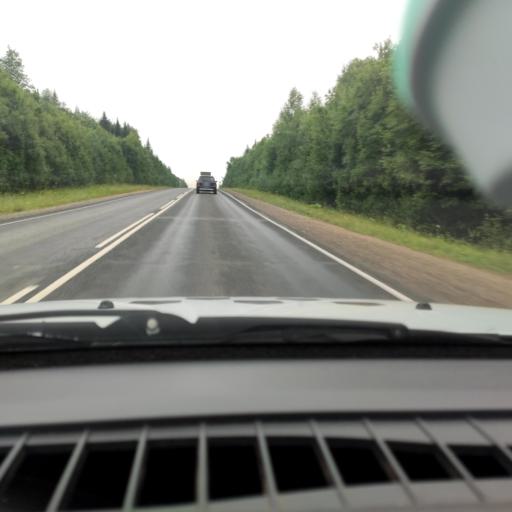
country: RU
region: Perm
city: Dobryanka
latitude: 58.5971
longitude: 56.6619
